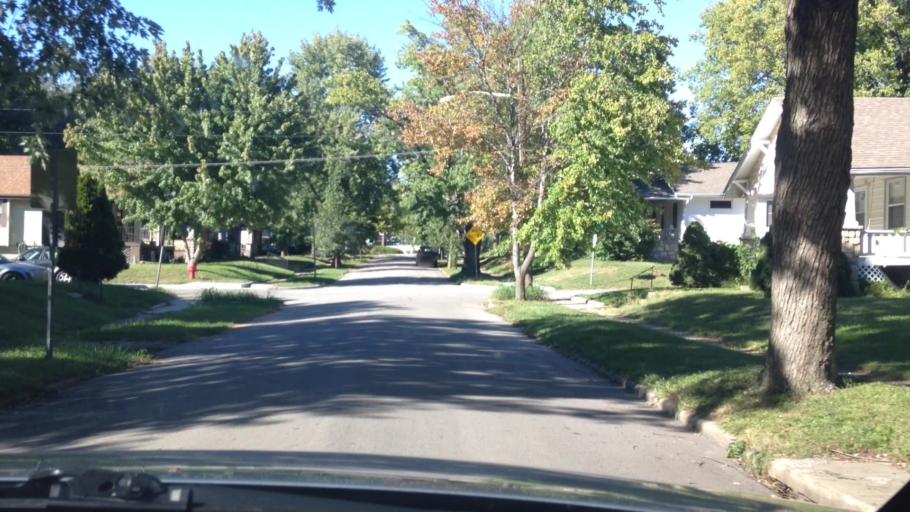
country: US
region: Kansas
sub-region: Johnson County
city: Westwood
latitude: 39.0486
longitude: -94.6130
